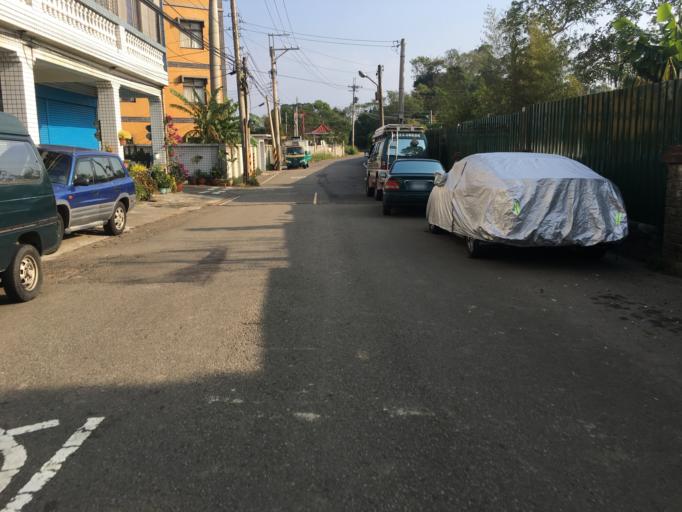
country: TW
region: Taiwan
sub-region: Hsinchu
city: Hsinchu
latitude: 24.7473
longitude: 121.0372
